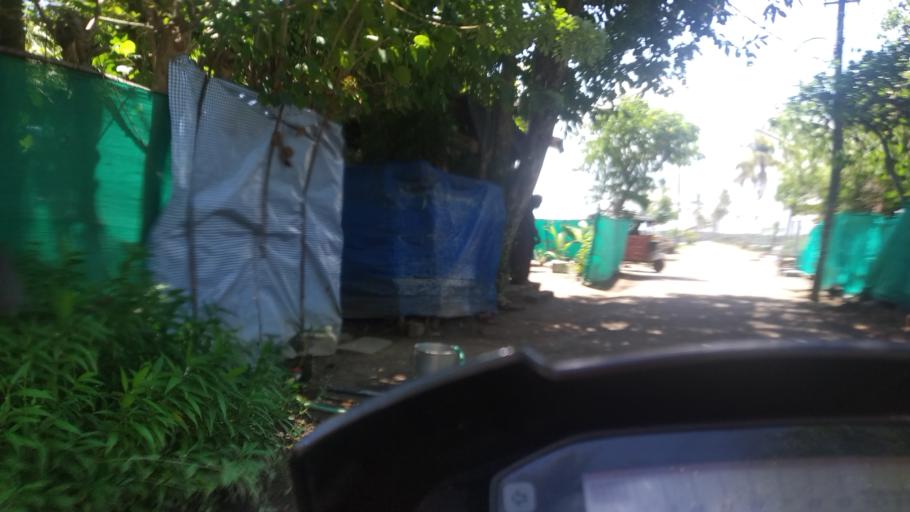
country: IN
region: Kerala
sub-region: Ernakulam
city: Elur
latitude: 10.0720
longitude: 76.2241
